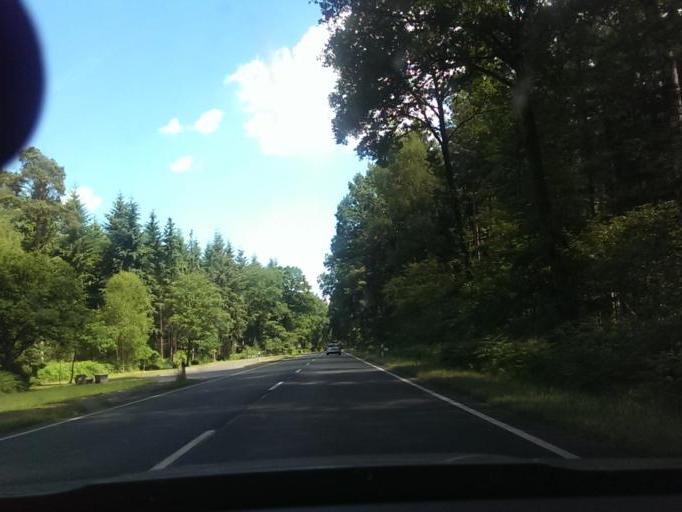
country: DE
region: Lower Saxony
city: Ahausen
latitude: 53.0251
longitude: 9.2877
